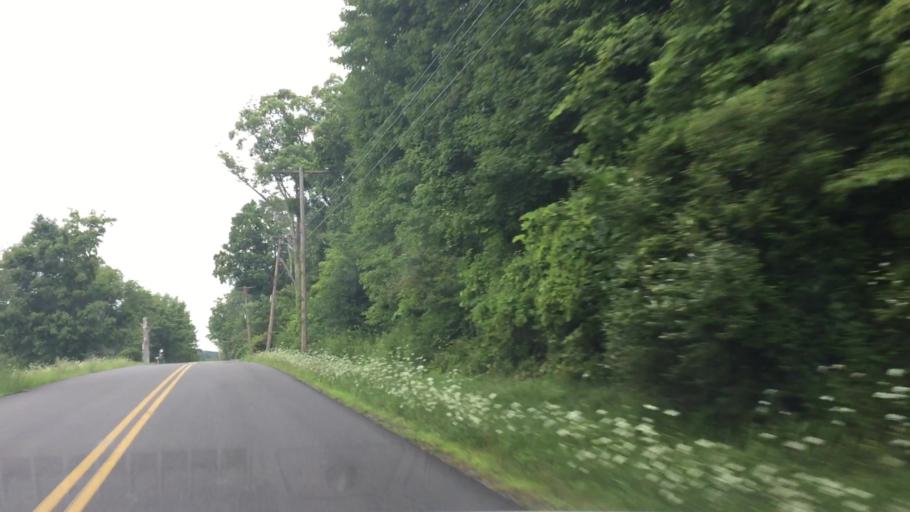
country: US
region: Massachusetts
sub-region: Berkshire County
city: Housatonic
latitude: 42.2678
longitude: -73.4094
